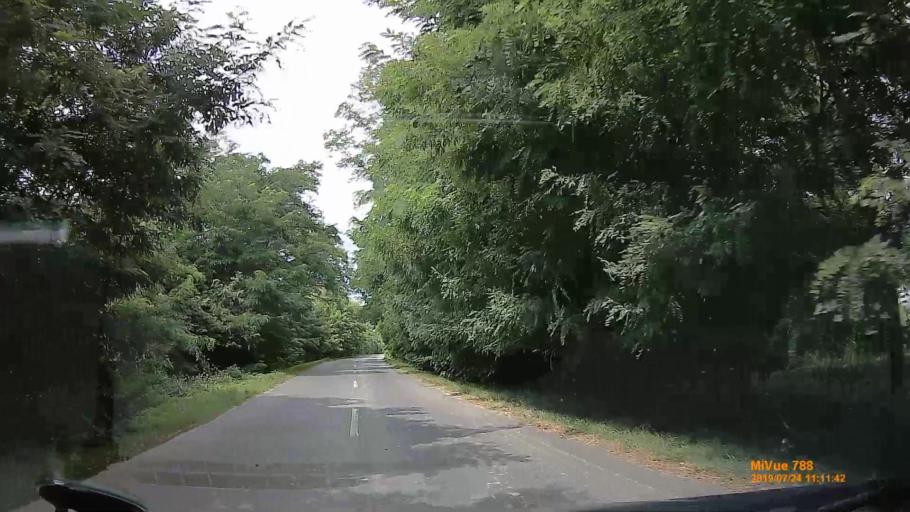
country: HU
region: Szabolcs-Szatmar-Bereg
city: Tarpa
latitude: 48.2035
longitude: 22.4683
